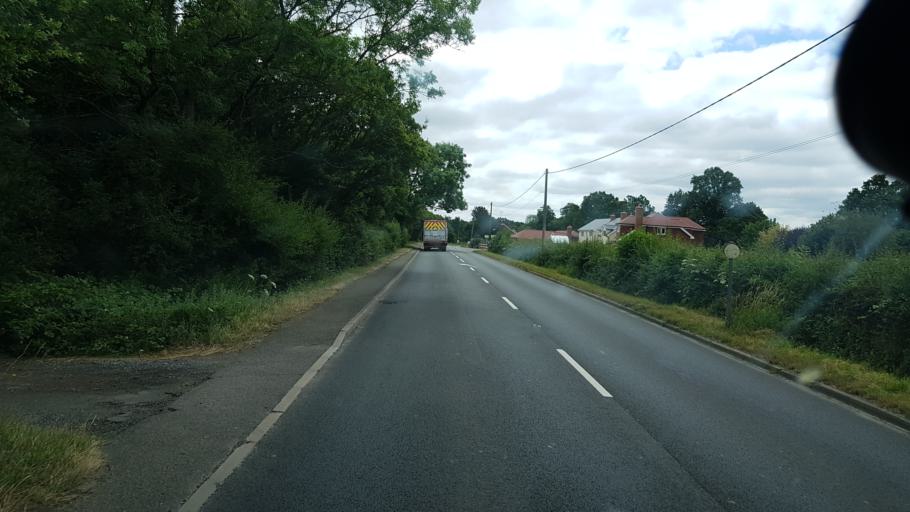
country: GB
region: England
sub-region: Surrey
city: Lingfield
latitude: 51.1867
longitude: -0.0478
